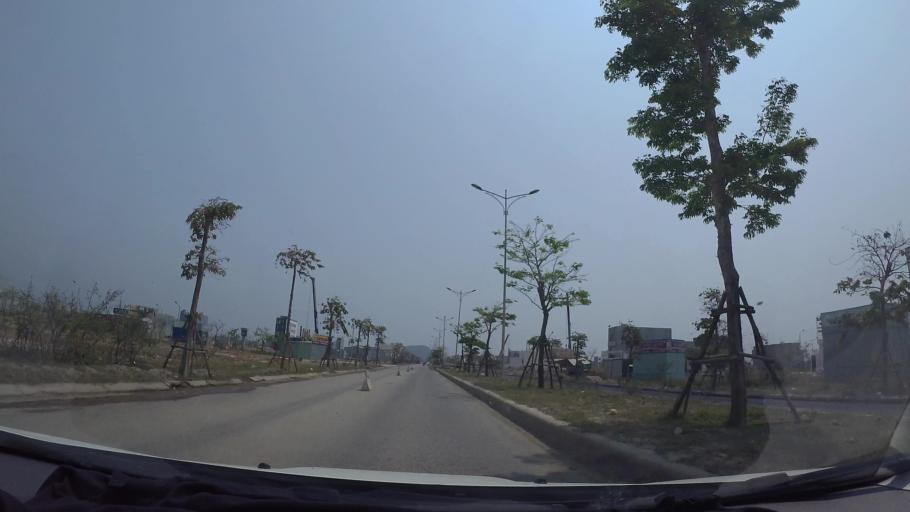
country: VN
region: Da Nang
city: Ngu Hanh Son
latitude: 16.0130
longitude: 108.2382
